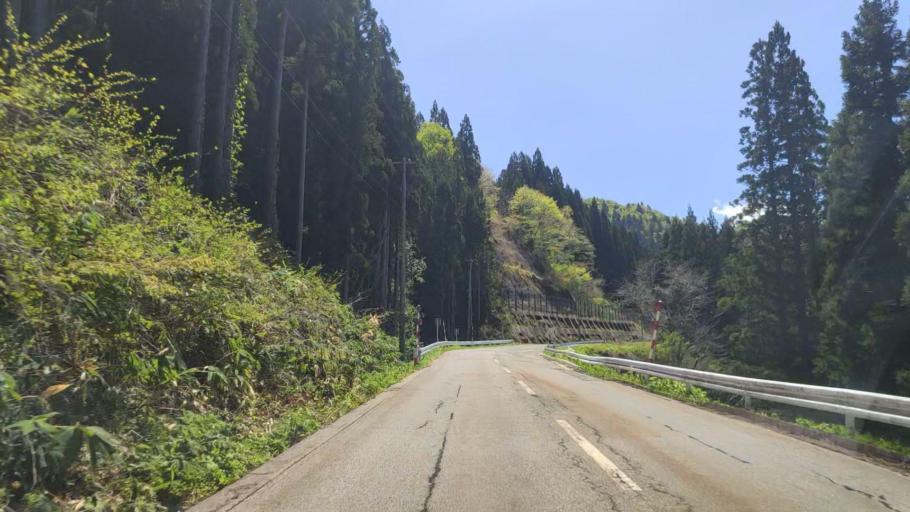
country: JP
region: Yamagata
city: Shinjo
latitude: 38.9705
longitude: 140.3538
